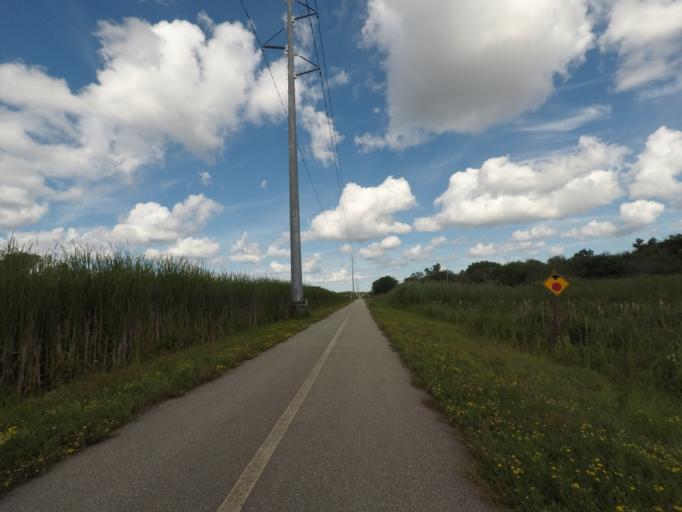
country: US
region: Wisconsin
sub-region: Waukesha County
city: Pewaukee
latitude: 43.0534
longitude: -88.2835
